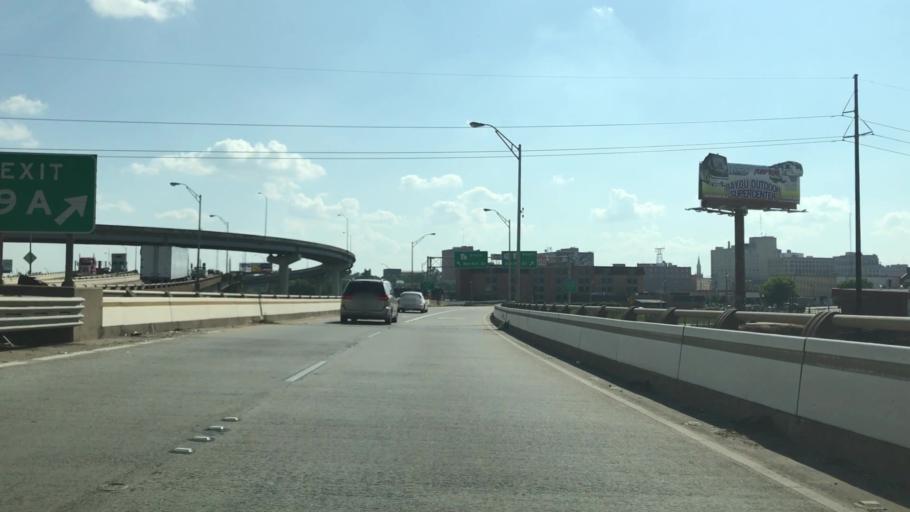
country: US
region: Louisiana
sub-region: Bossier Parish
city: Bossier City
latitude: 32.5115
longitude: -93.7407
